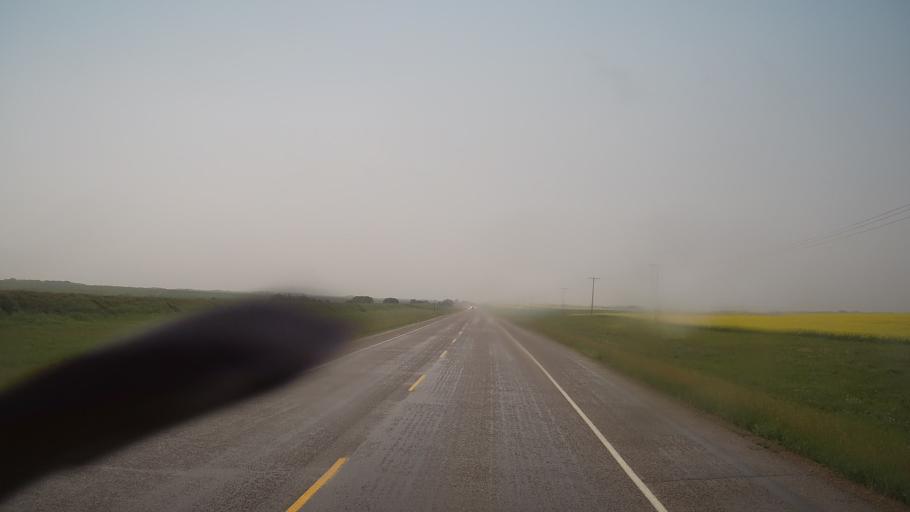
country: CA
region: Saskatchewan
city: Biggar
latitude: 52.1442
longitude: -108.2012
